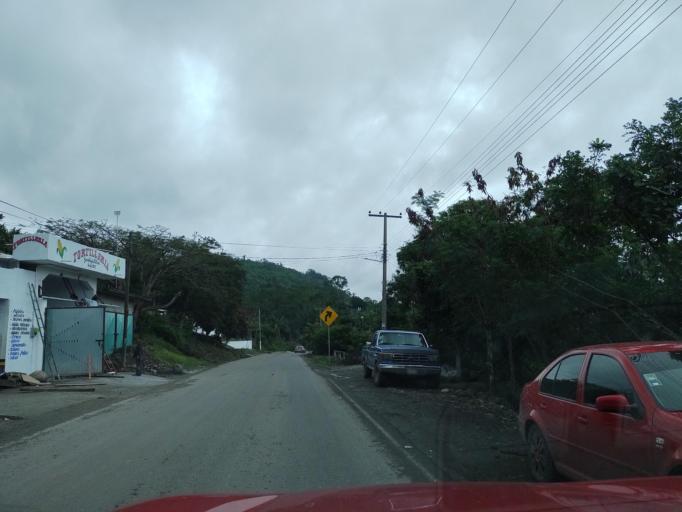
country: MX
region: Puebla
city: Espinal
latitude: 20.2618
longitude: -97.3719
